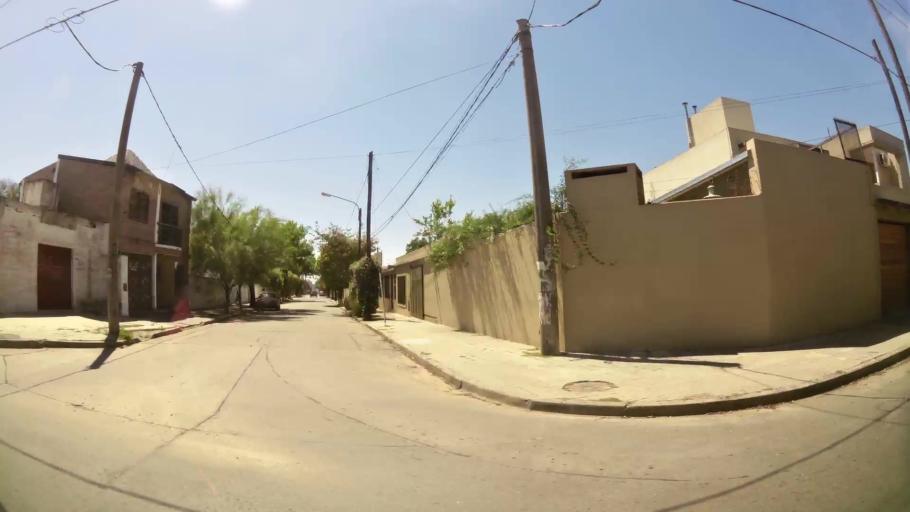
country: AR
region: Cordoba
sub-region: Departamento de Capital
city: Cordoba
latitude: -31.4257
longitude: -64.2098
